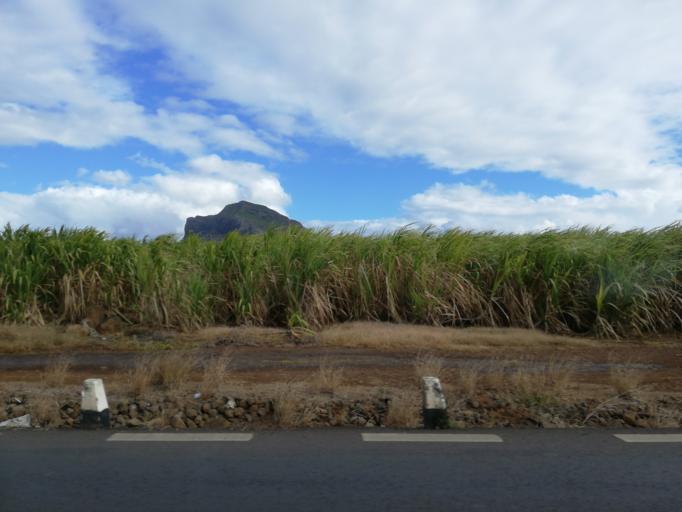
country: MU
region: Black River
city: Gros Cailloux
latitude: -20.2307
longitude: 57.4483
